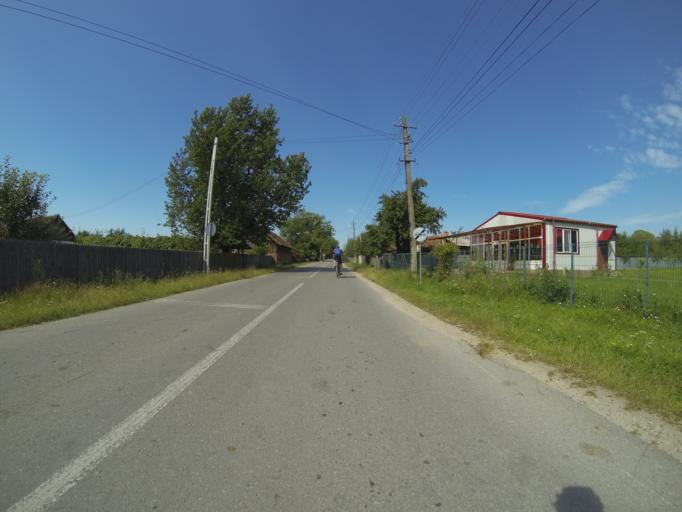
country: RO
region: Gorj
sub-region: Comuna Polovragi
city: Polovragi
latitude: 45.1675
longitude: 23.8167
